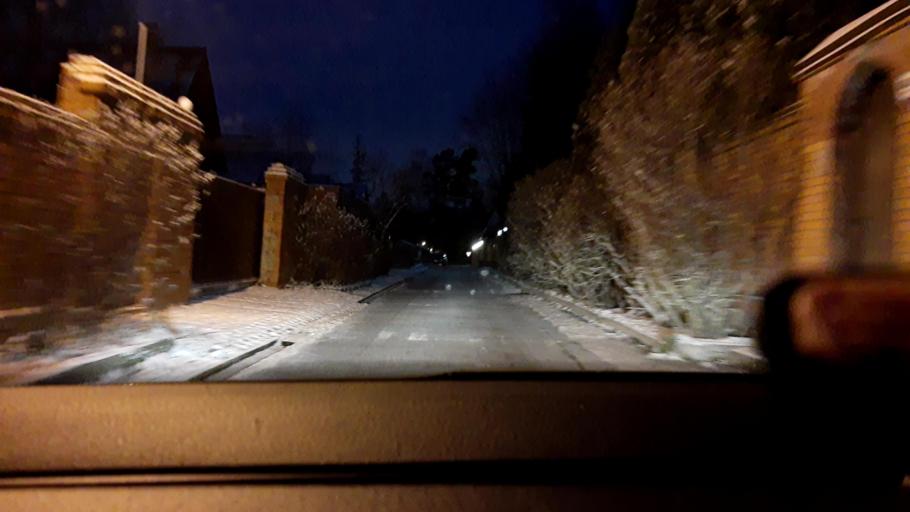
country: RU
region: Moskovskaya
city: Cherkizovo
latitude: 55.9853
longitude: 37.7792
